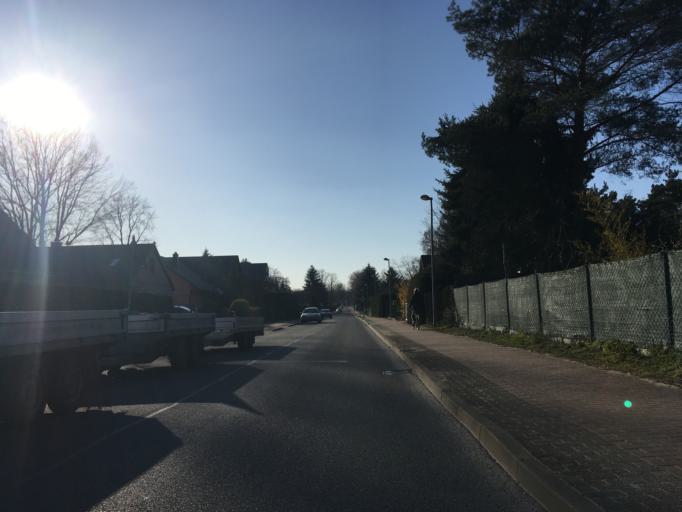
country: DE
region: Berlin
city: Buch
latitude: 52.6375
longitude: 13.5296
